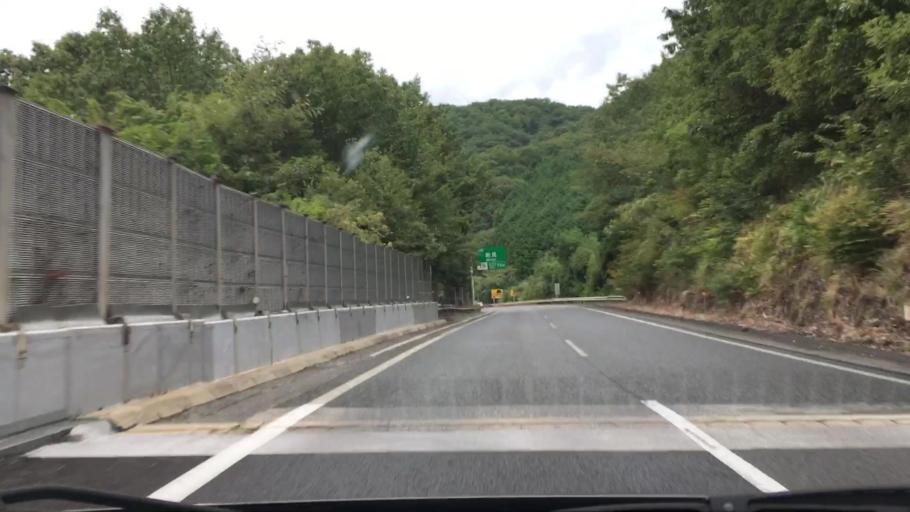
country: JP
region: Okayama
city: Niimi
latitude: 34.9911
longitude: 133.4597
